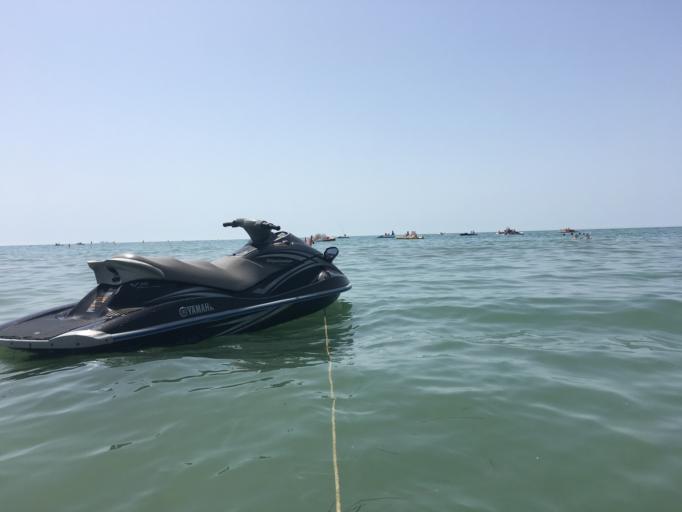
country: AL
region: Tirane
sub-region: Rrethi i Kavajes
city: Golem
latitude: 41.2648
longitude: 19.5180
